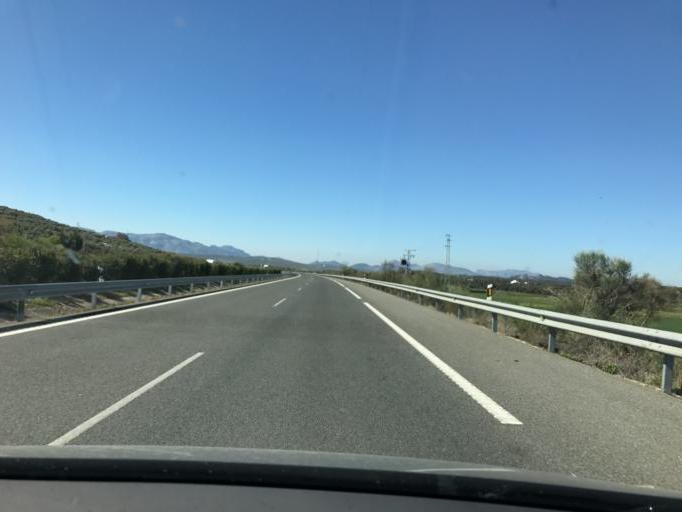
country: ES
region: Andalusia
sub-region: Provincia de Malaga
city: Villanueva de Tapia
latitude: 37.1082
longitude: -4.3098
